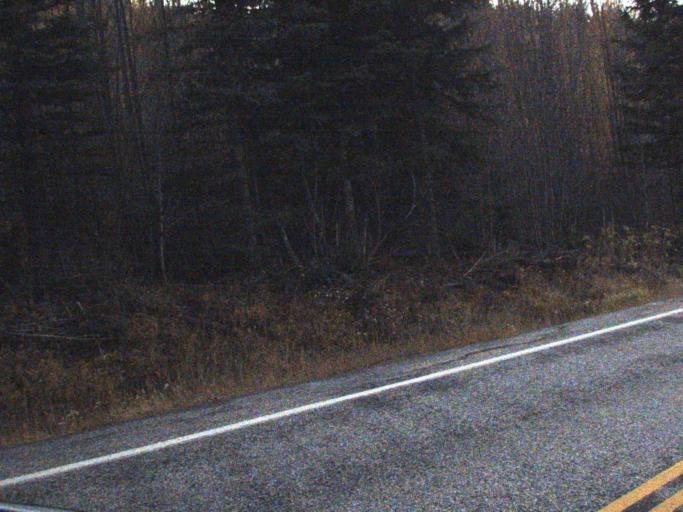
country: US
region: Washington
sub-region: Ferry County
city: Republic
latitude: 48.5955
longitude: -118.5164
